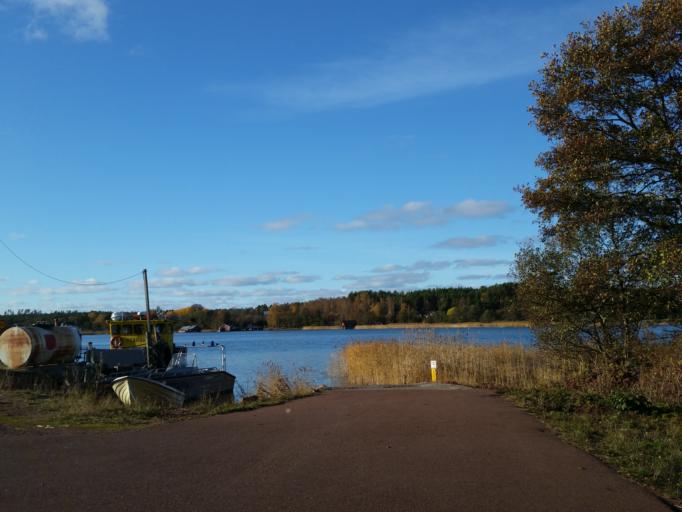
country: AX
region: Alands landsbygd
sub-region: Geta
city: Geta
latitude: 60.3662
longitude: 19.7693
